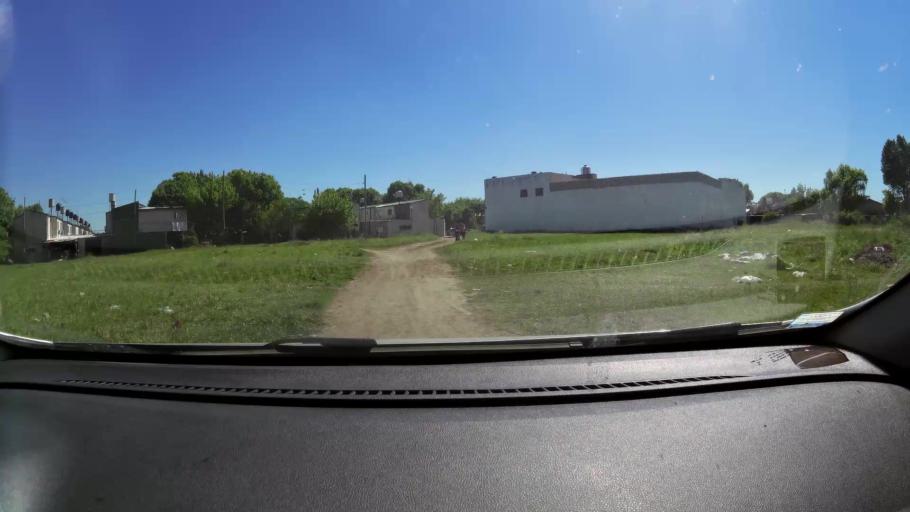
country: AR
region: Santa Fe
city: Perez
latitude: -32.9745
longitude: -60.7054
